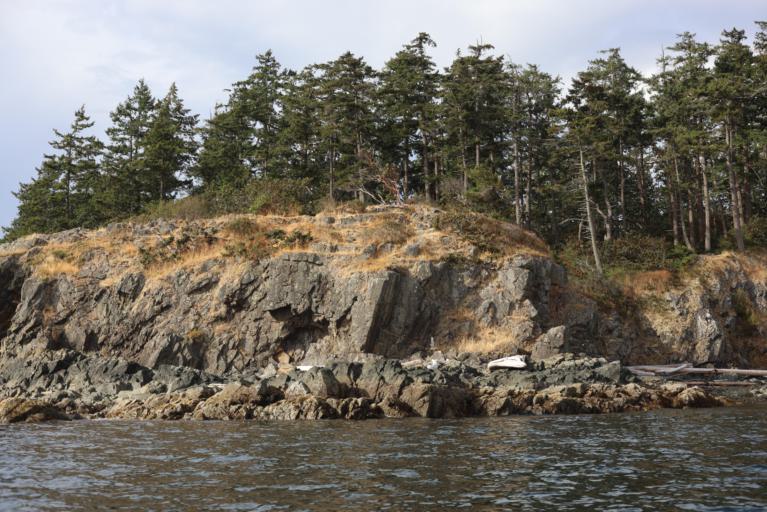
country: CA
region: British Columbia
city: Nanaimo
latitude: 49.2292
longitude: -123.9480
